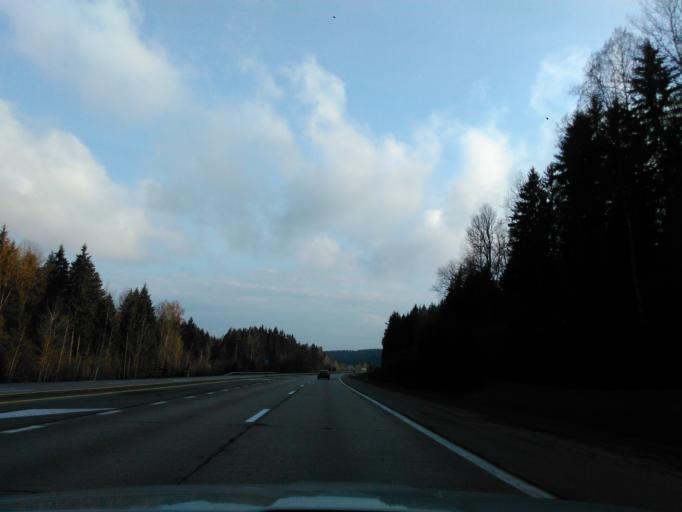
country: BY
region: Minsk
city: Lahoysk
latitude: 54.1214
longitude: 27.8071
